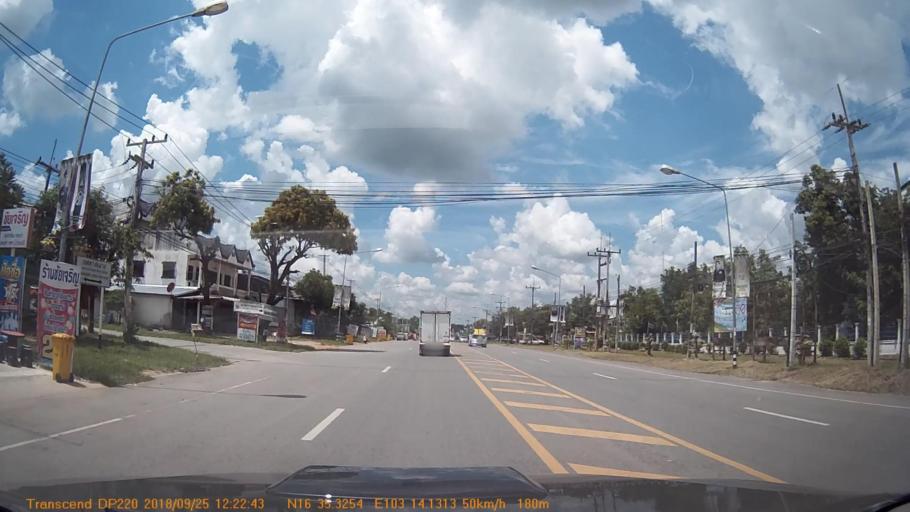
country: TH
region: Kalasin
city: Huai Mek
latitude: 16.5888
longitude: 103.2354
